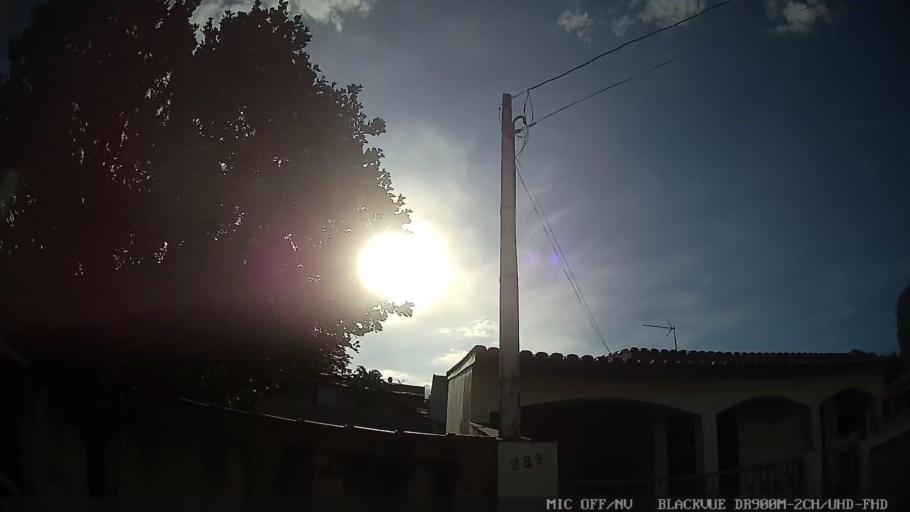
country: BR
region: Sao Paulo
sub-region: Serra Negra
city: Serra Negra
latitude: -22.6770
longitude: -46.6809
